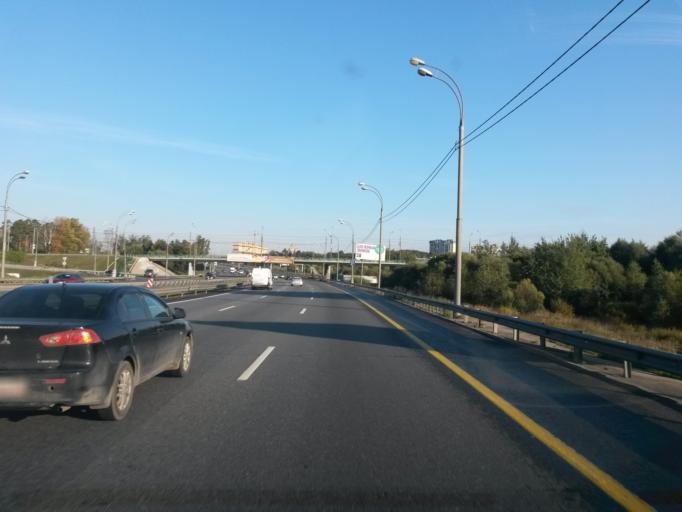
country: RU
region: Moskovskaya
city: Vidnoye
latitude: 55.5417
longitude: 37.6969
